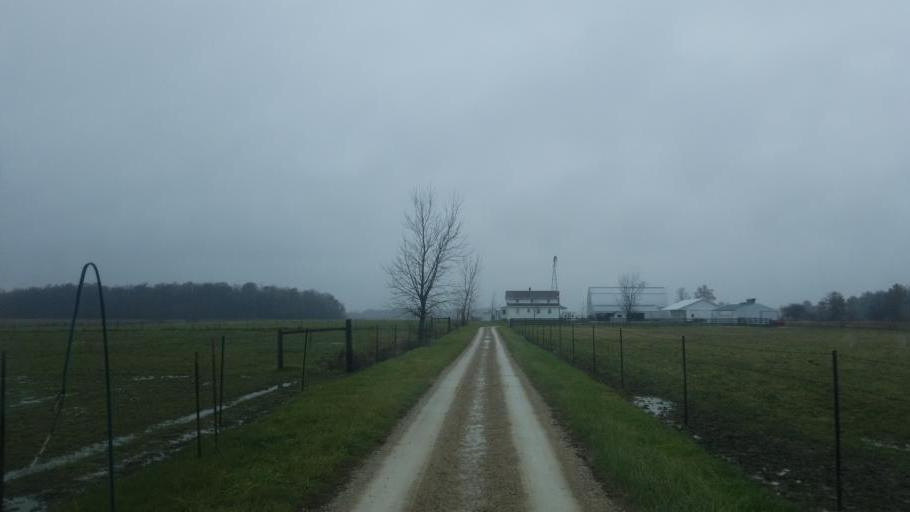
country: US
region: Indiana
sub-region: Adams County
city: Berne
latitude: 40.6307
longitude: -84.8862
